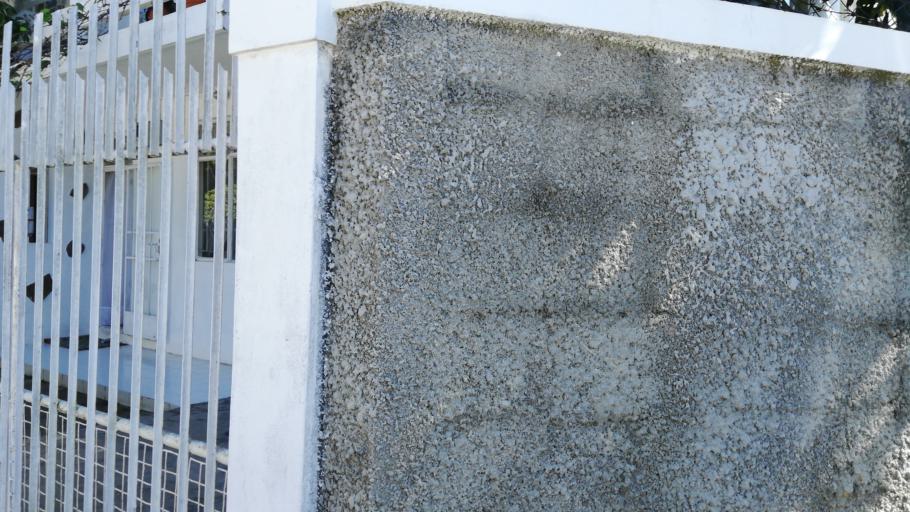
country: MU
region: Plaines Wilhems
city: Ebene
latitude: -20.2337
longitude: 57.4756
